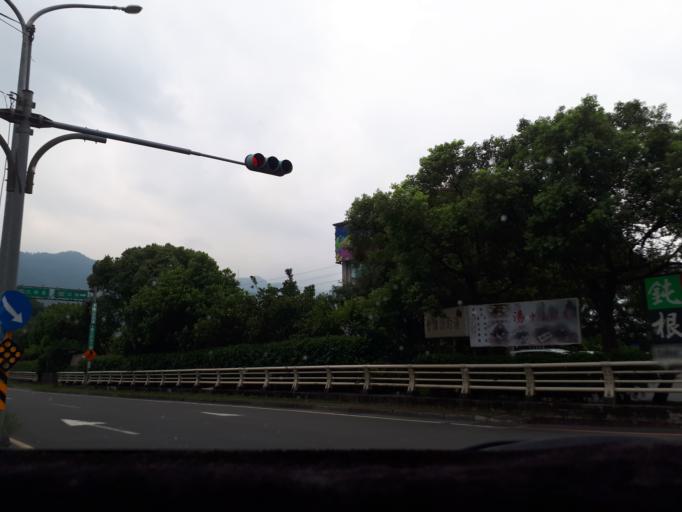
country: TW
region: Taipei
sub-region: Taipei
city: Banqiao
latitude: 24.9598
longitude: 121.5045
